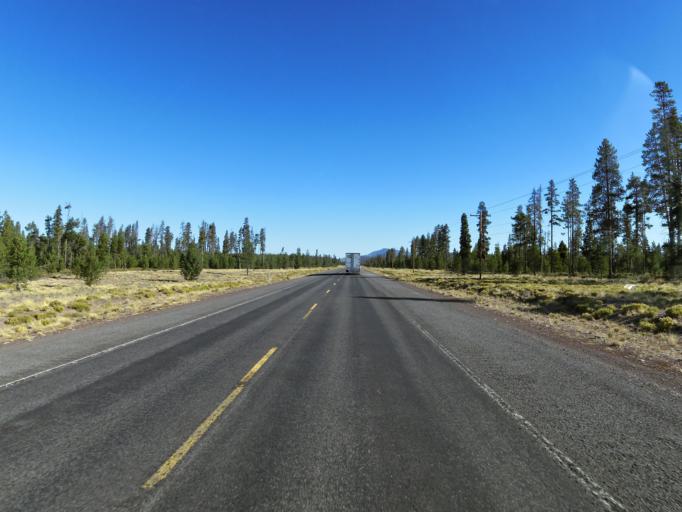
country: US
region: Oregon
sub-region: Deschutes County
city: La Pine
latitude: 43.1582
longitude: -121.7930
